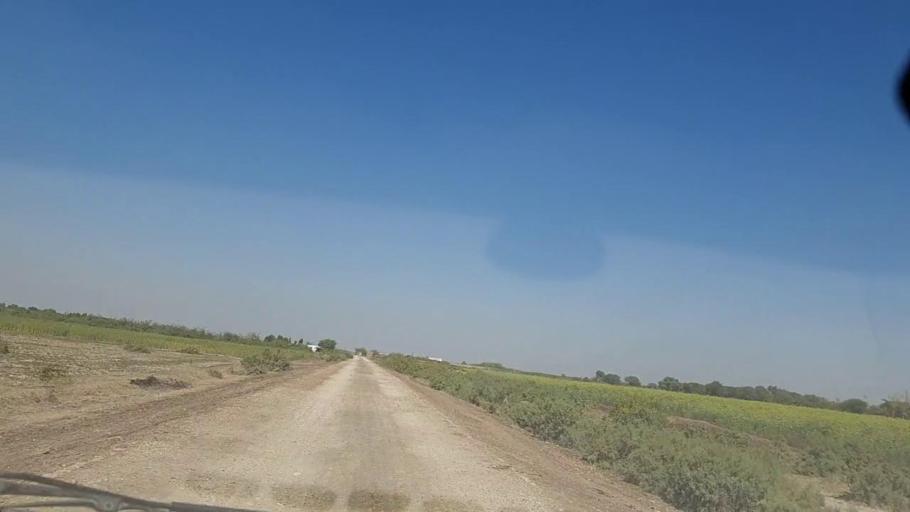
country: PK
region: Sindh
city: Mirpur Khas
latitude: 25.4314
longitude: 69.0439
